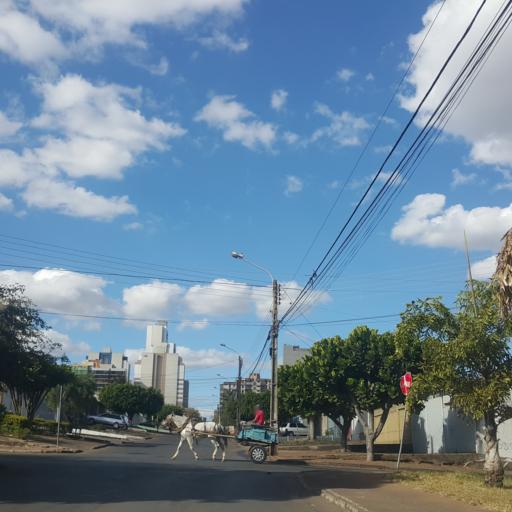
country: BR
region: Federal District
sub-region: Brasilia
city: Brasilia
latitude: -15.8256
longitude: -48.0654
